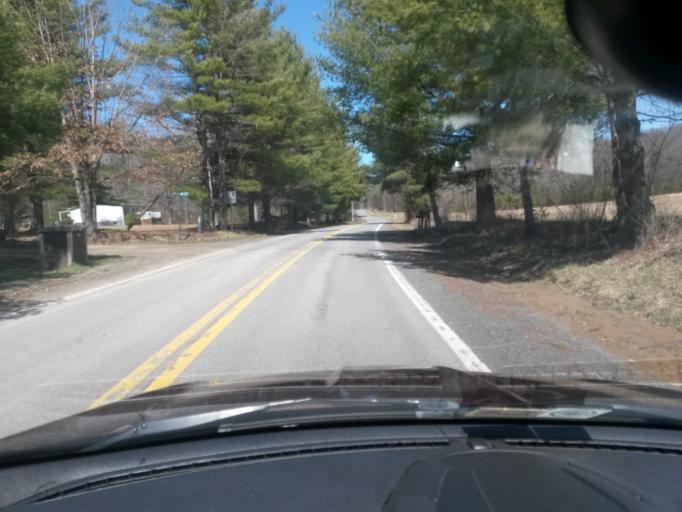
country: US
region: West Virginia
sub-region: Greenbrier County
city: White Sulphur Springs
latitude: 37.6338
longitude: -80.3402
